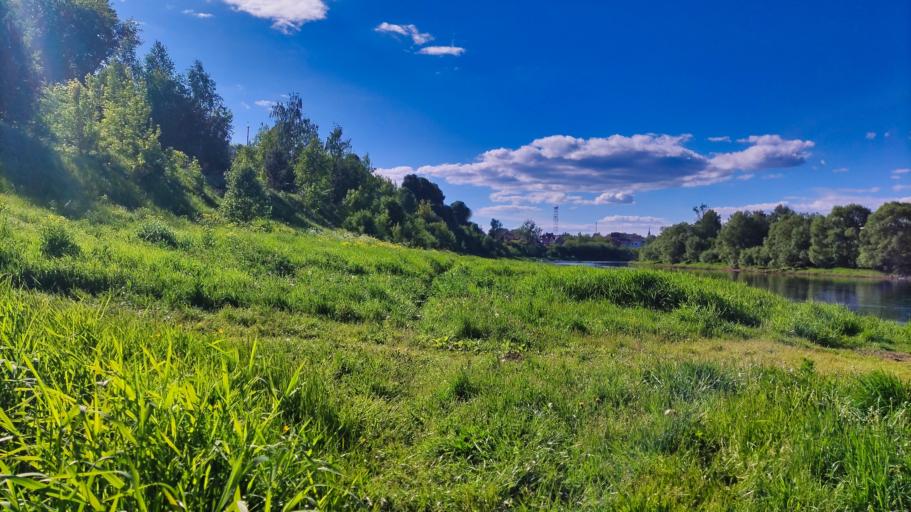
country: RU
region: Tverskaya
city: Rzhev
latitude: 56.2520
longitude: 34.3452
